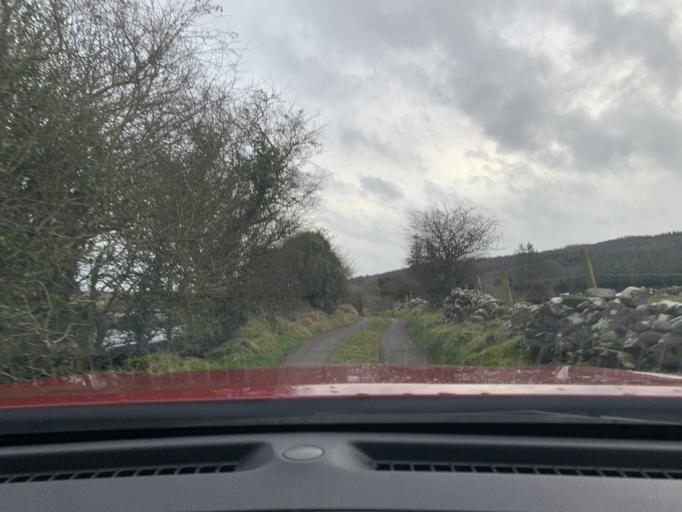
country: IE
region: Connaught
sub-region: Sligo
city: Ballymote
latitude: 53.9715
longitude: -8.4731
